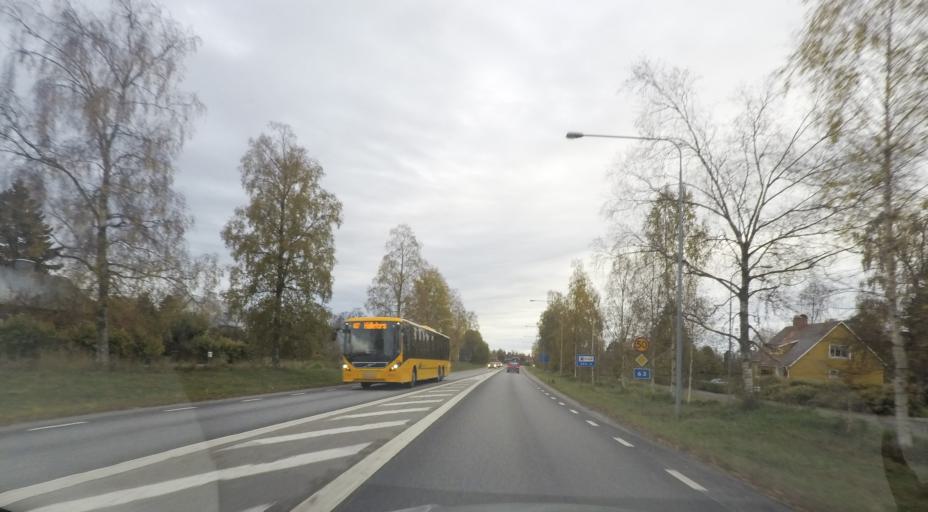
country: SE
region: OErebro
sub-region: Hallefors Kommun
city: Haellefors
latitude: 59.7843
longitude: 14.5323
